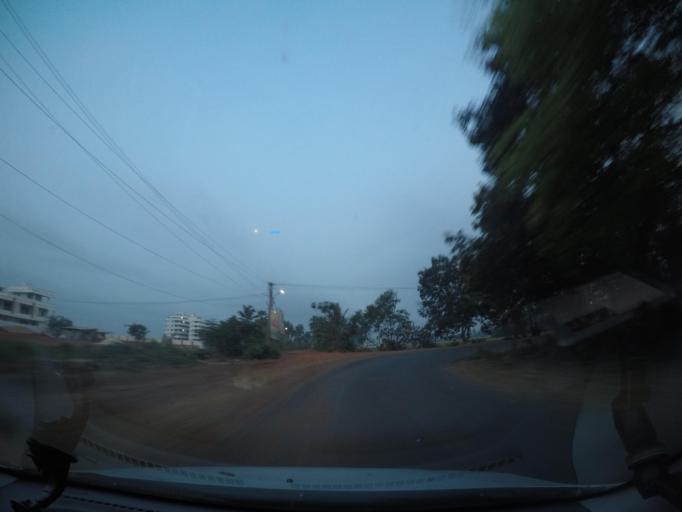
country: IN
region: Andhra Pradesh
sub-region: West Godavari
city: Tadepallegudem
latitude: 16.8152
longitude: 81.4071
